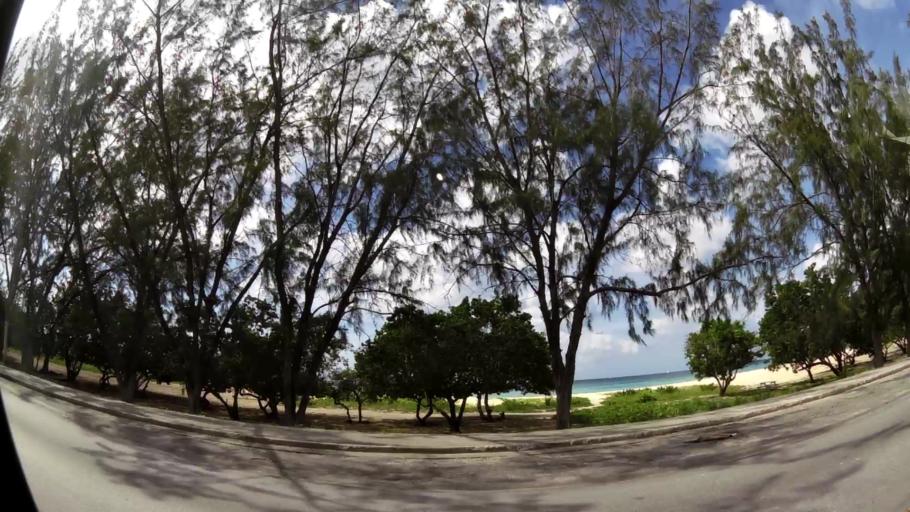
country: BB
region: Saint Michael
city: Bridgetown
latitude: 13.1157
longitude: -59.6269
